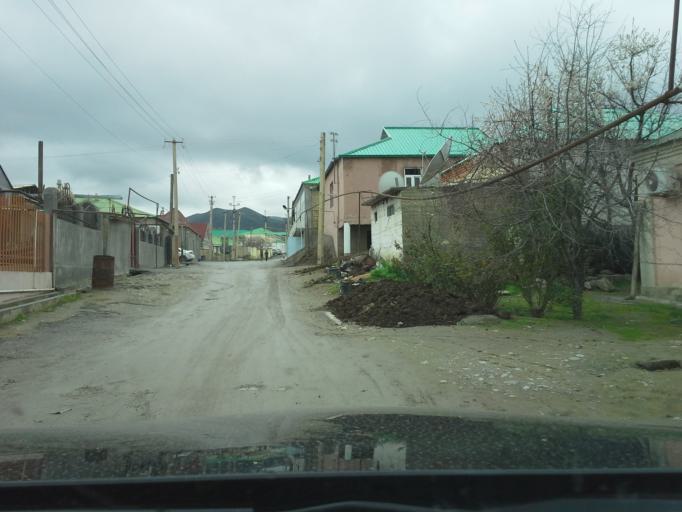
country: TM
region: Ahal
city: Abadan
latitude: 37.9577
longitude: 58.2112
